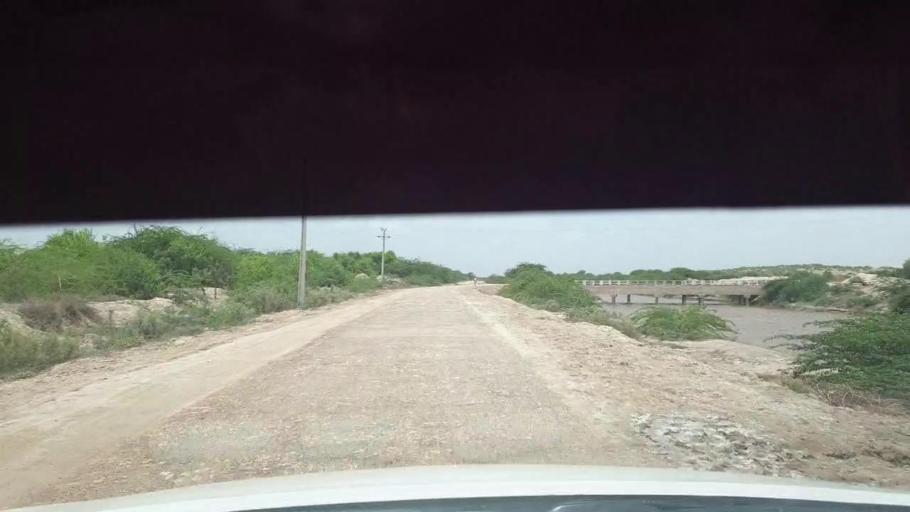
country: PK
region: Sindh
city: Kadhan
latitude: 24.5300
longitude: 69.1267
